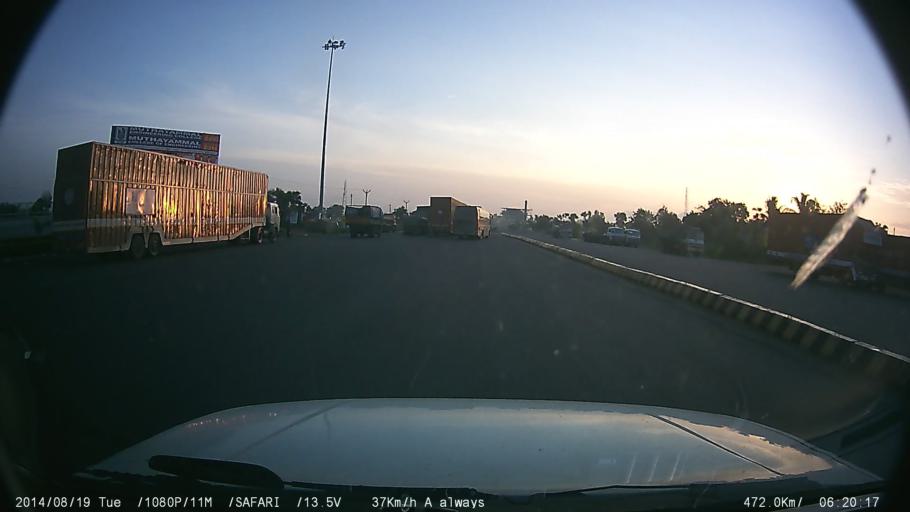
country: IN
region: Tamil Nadu
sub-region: Dharmapuri
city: Dharmapuri
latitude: 12.0070
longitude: 78.0810
